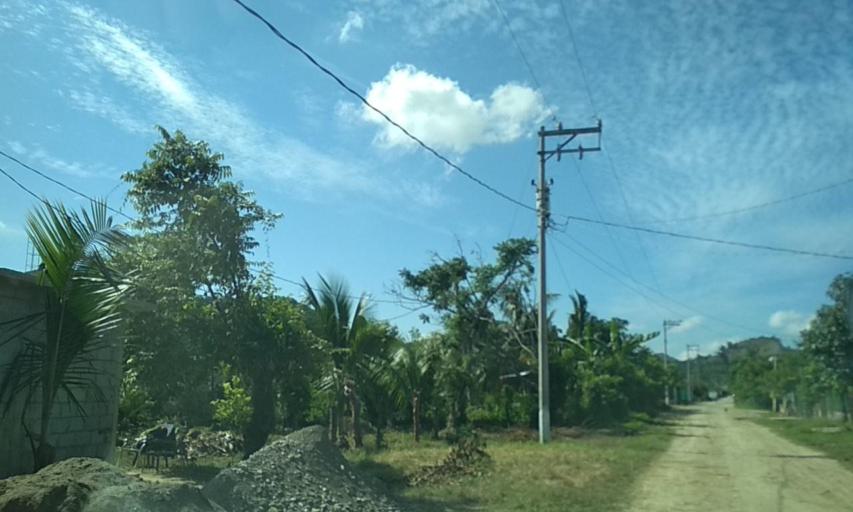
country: MX
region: Veracruz
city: Cazones de Herrera
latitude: 20.6487
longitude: -97.3008
